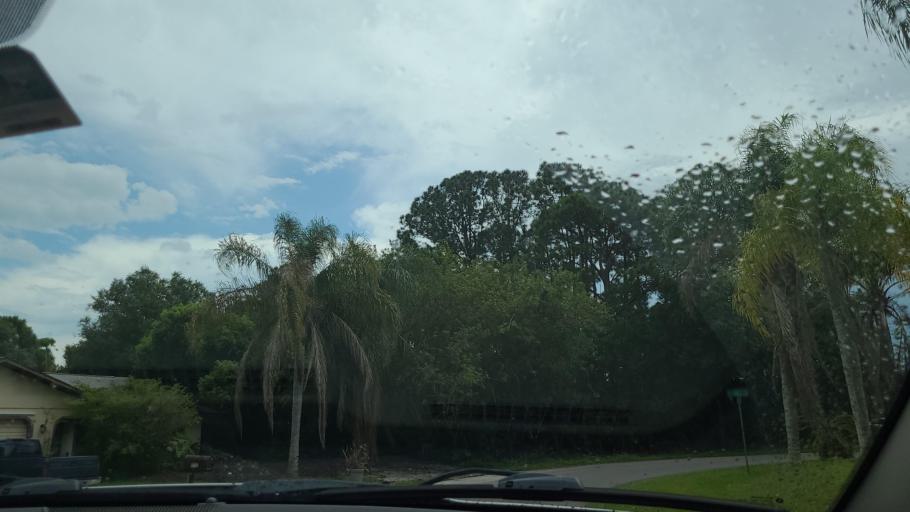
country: US
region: Florida
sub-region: Brevard County
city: Grant-Valkaria
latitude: 27.9467
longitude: -80.6411
